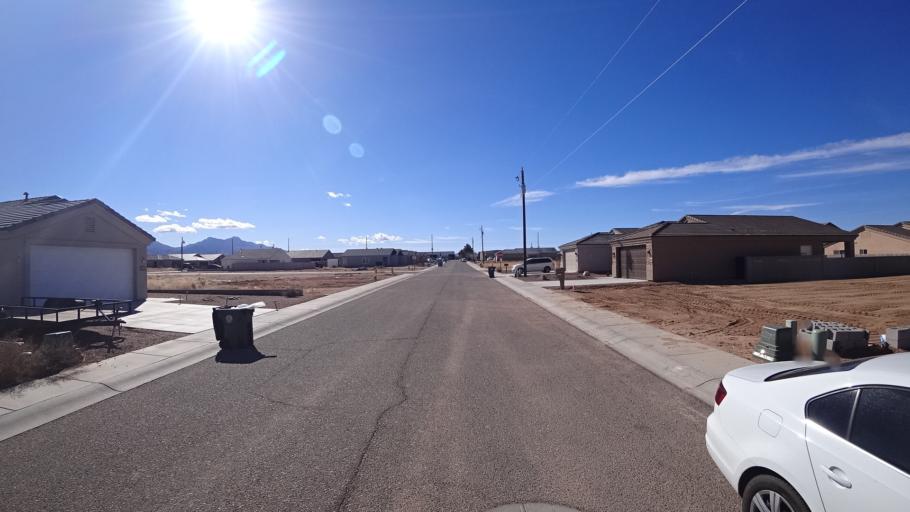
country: US
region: Arizona
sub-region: Mohave County
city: New Kingman-Butler
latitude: 35.2272
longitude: -114.0224
